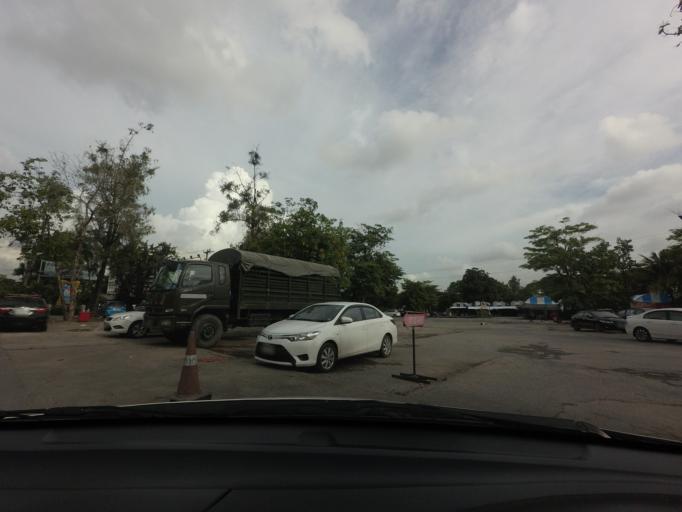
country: TH
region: Bangkok
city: Chatuchak
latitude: 13.8159
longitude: 100.5530
